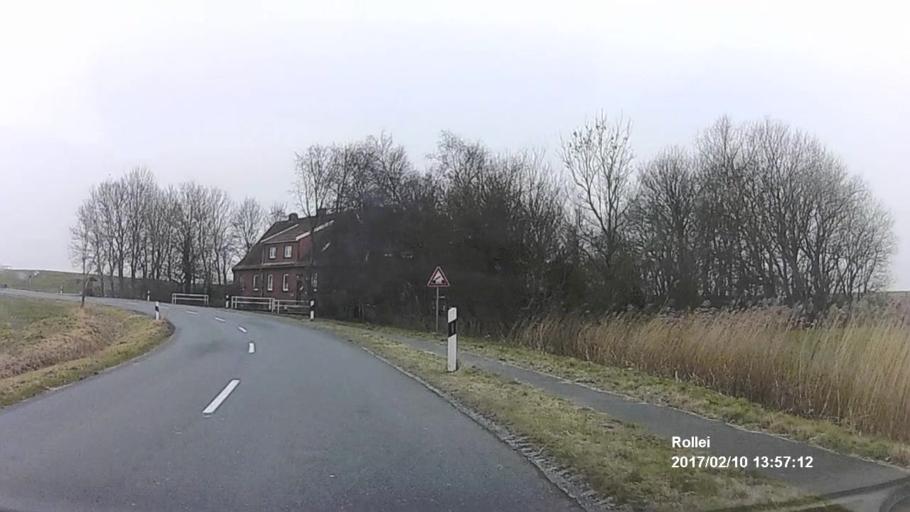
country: DE
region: Lower Saxony
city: Norddeich
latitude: 53.5439
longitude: 7.1434
